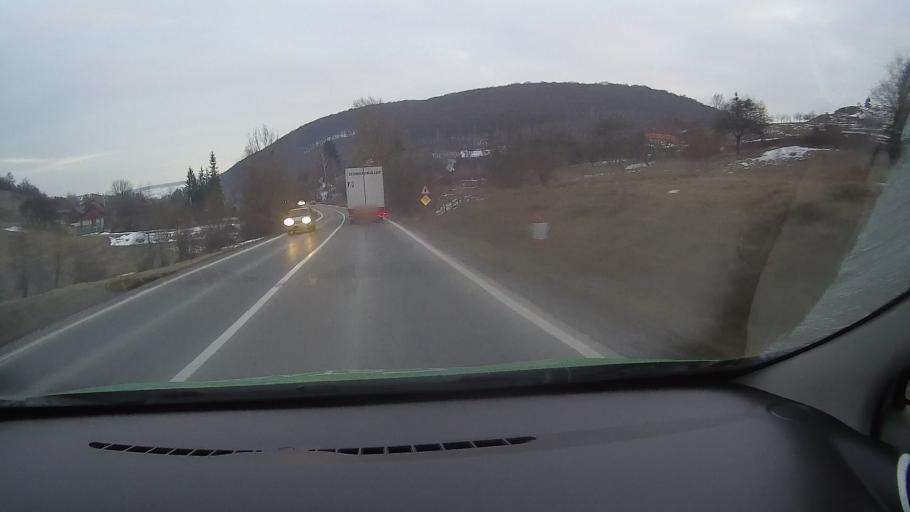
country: RO
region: Harghita
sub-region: Municipiul Odorheiu Secuiesc
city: Odorheiu Secuiesc
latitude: 46.3372
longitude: 25.2700
